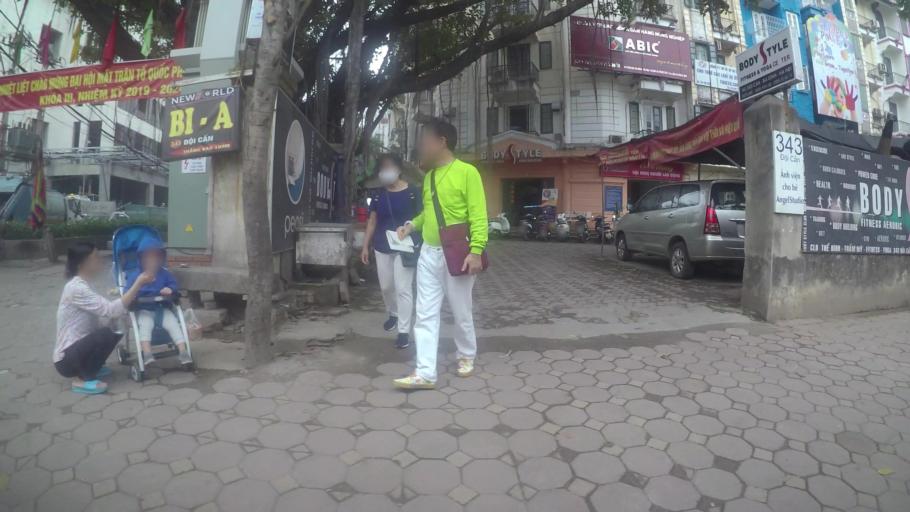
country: VN
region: Ha Noi
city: Cau Giay
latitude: 21.0361
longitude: 105.8171
